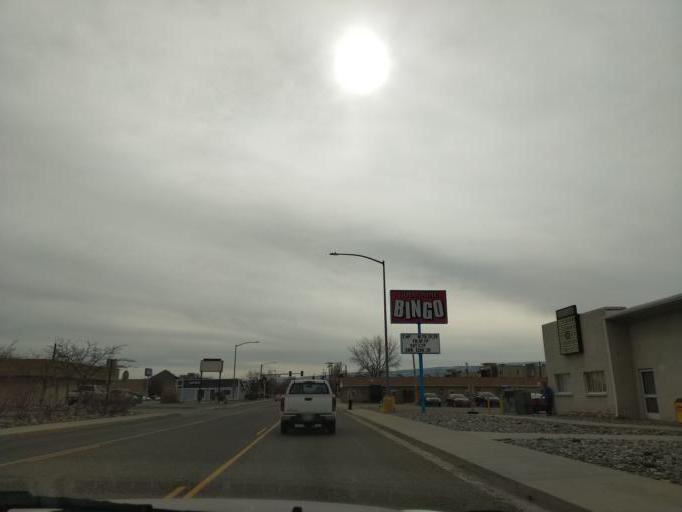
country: US
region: Colorado
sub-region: Mesa County
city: Grand Junction
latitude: 39.0788
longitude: -108.5292
